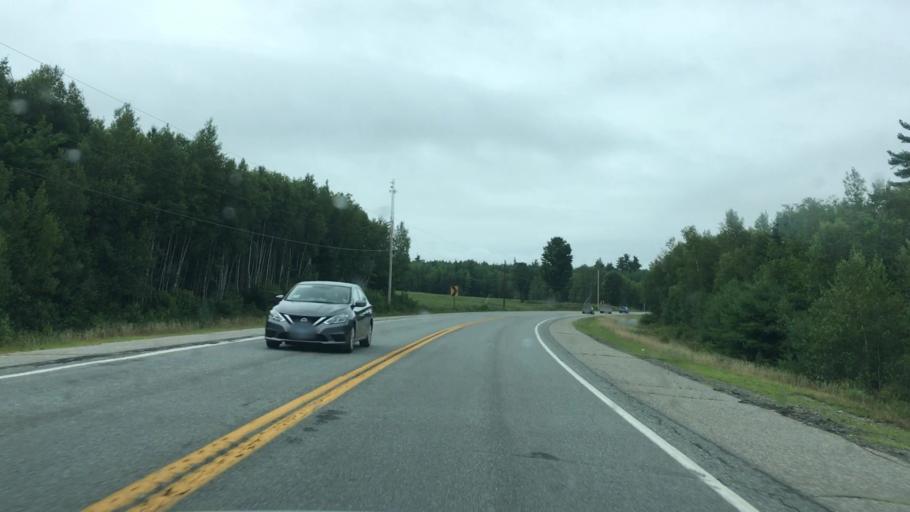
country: US
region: Maine
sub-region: Washington County
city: Cherryfield
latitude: 44.8539
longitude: -68.0580
